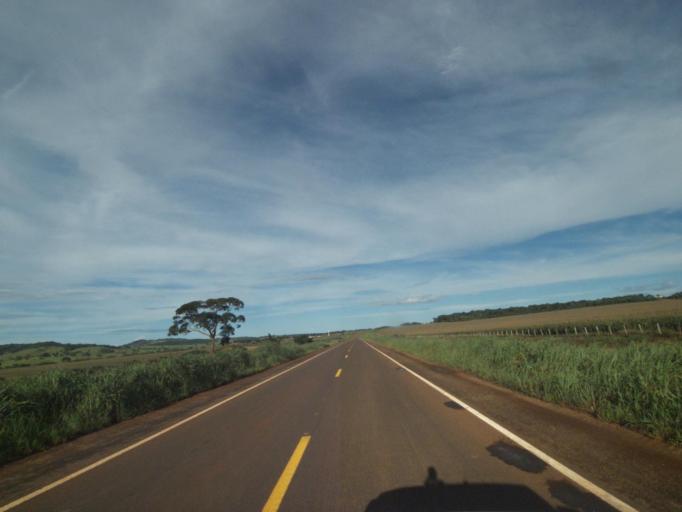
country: BR
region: Goias
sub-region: Jaragua
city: Jaragua
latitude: -15.9048
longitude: -49.5478
